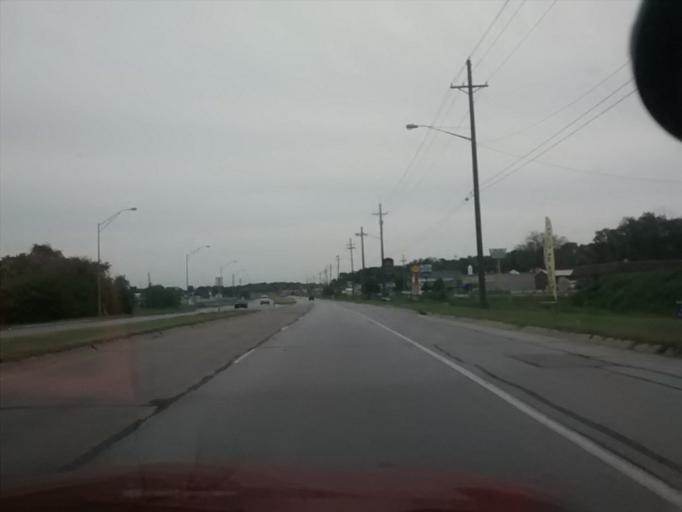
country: US
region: Nebraska
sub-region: Sarpy County
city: Offutt Air Force Base
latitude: 41.1619
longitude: -95.9251
